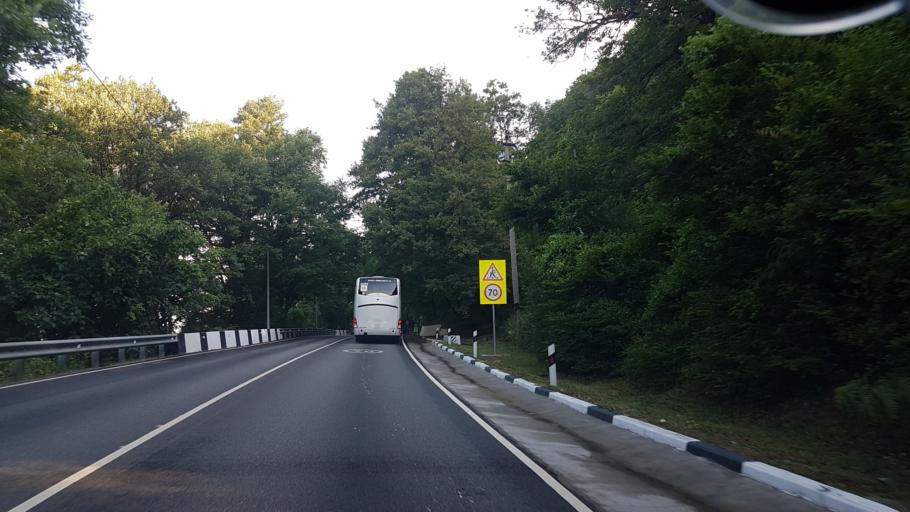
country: RU
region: Krasnodarskiy
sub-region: Sochi City
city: Lazarevskoye
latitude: 43.8426
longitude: 39.4140
